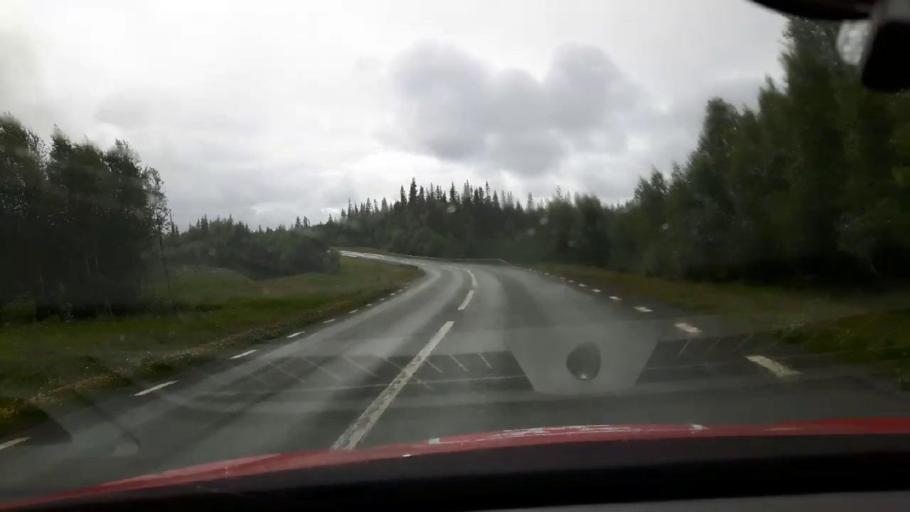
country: SE
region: Jaemtland
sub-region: Are Kommun
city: Are
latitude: 63.3062
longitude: 12.4302
